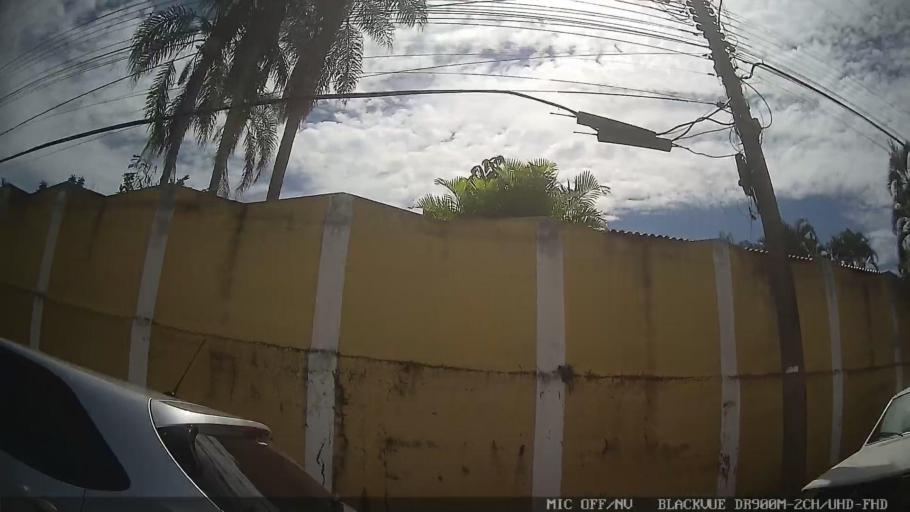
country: BR
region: Sao Paulo
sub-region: Laranjal Paulista
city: Laranjal Paulista
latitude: -23.0335
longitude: -47.8369
